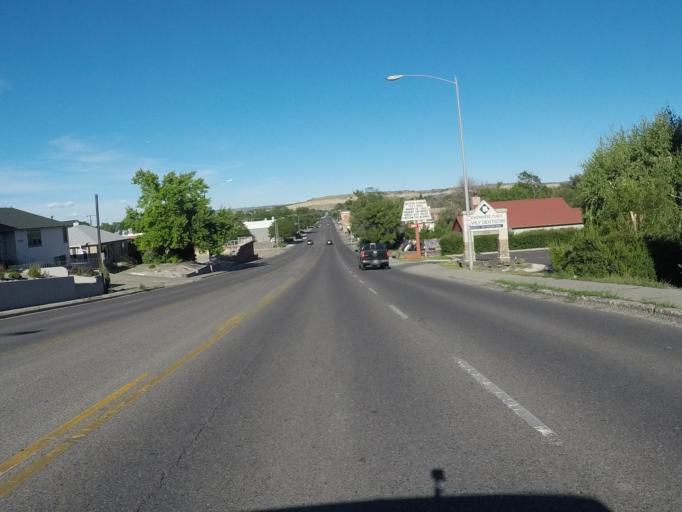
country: US
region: Montana
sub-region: Yellowstone County
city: Billings
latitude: 45.7770
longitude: -108.5432
